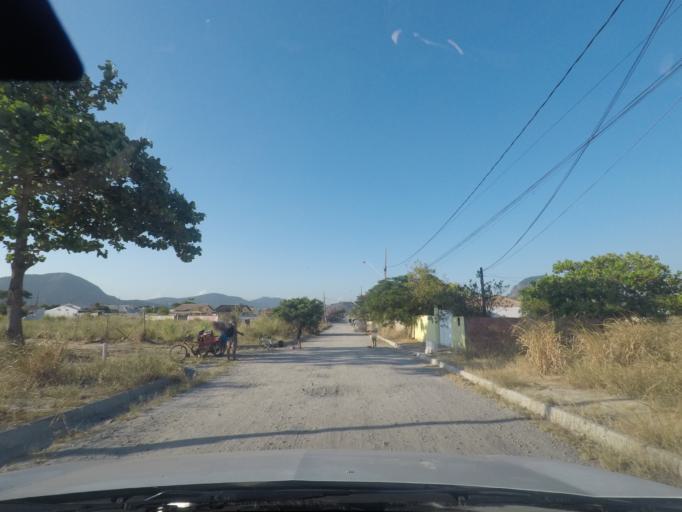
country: BR
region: Rio de Janeiro
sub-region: Marica
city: Marica
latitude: -22.9663
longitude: -42.9351
